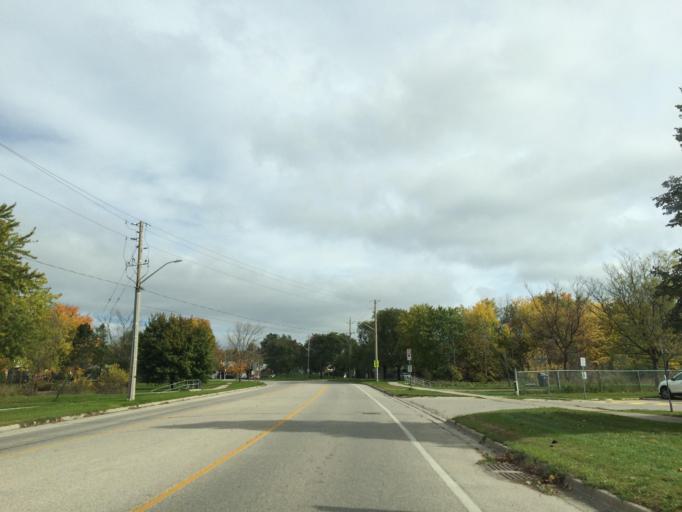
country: CA
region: Ontario
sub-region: Wellington County
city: Guelph
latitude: 43.5278
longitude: -80.2942
